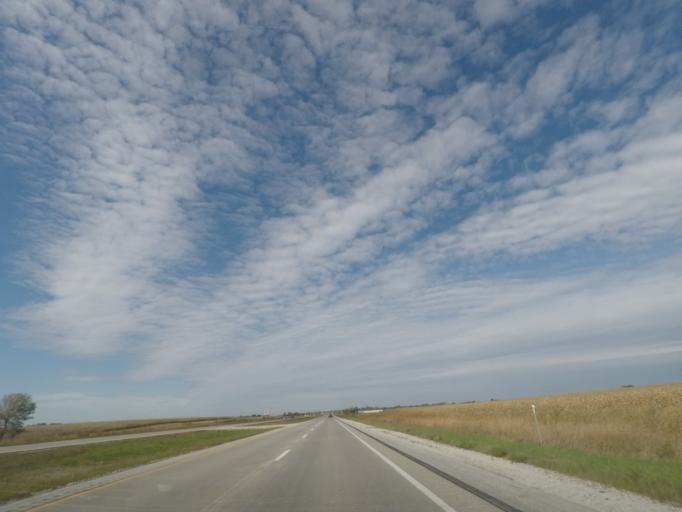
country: US
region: Iowa
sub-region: Story County
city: Ames
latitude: 42.0164
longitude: -93.7048
